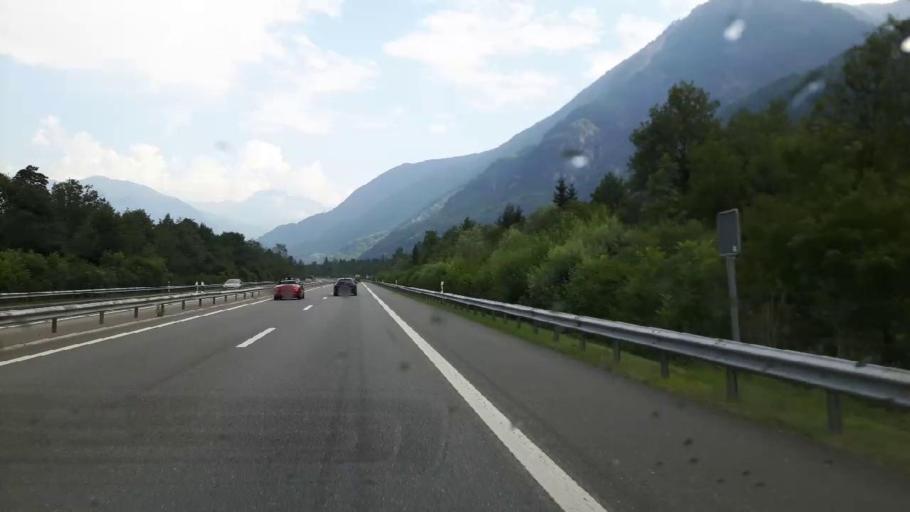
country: CH
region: Ticino
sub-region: Riviera District
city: Lodrino
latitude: 46.2841
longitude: 8.9929
